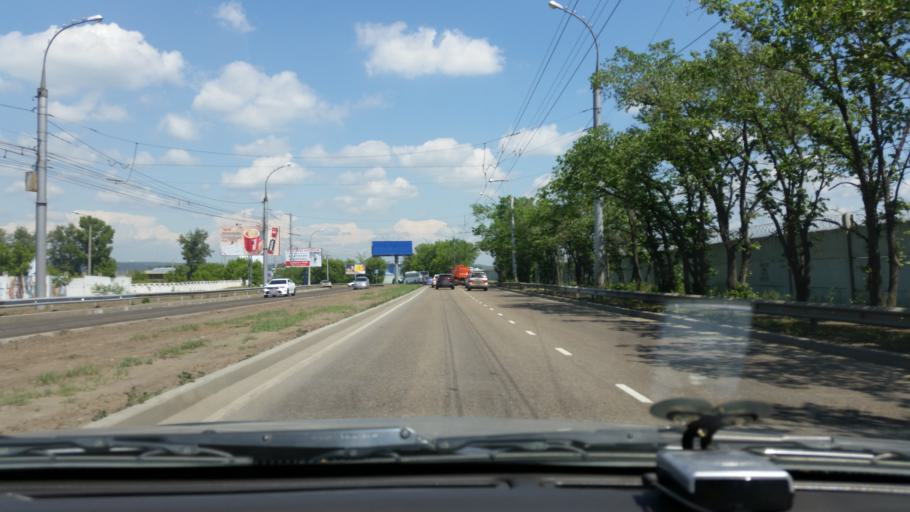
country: RU
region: Irkutsk
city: Dzerzhinsk
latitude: 52.2686
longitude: 104.3482
